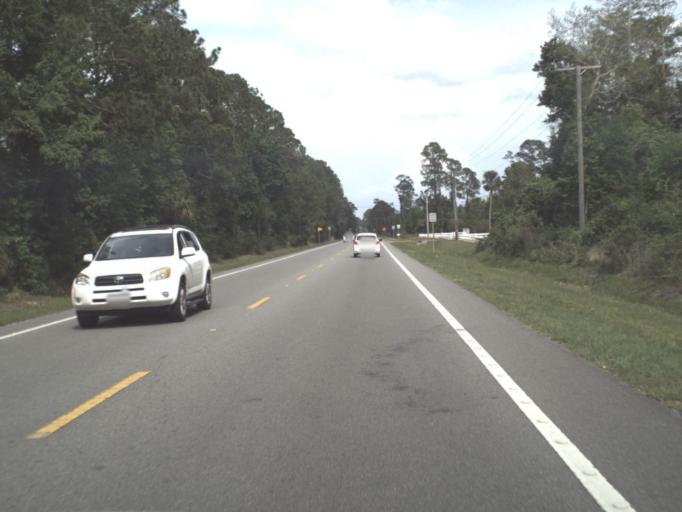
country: US
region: Florida
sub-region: Flagler County
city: Bunnell
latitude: 29.4669
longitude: -81.2830
